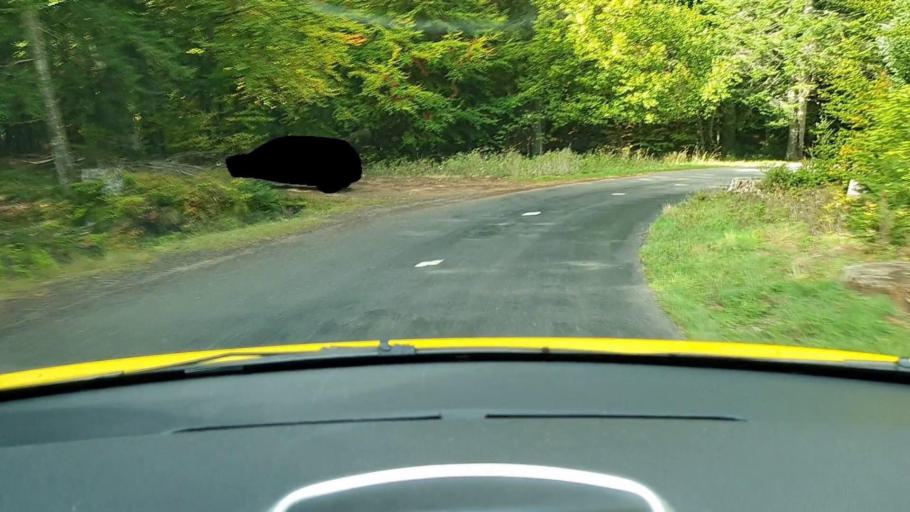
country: FR
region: Languedoc-Roussillon
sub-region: Departement du Gard
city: Valleraugue
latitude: 44.0763
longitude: 3.5637
